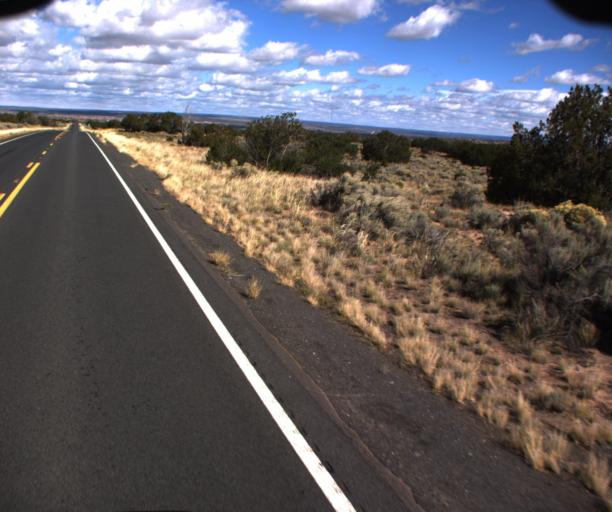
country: US
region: Arizona
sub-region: Apache County
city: Houck
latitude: 35.1435
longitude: -109.3330
